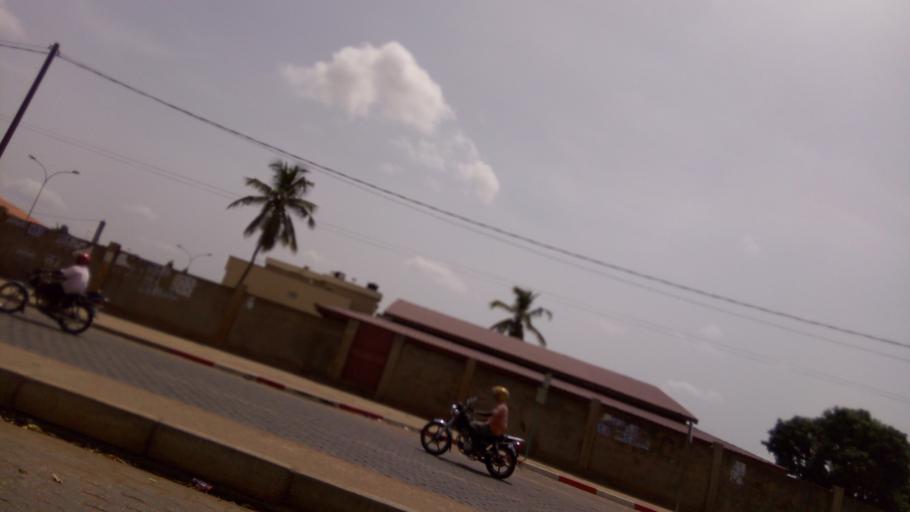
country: TG
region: Maritime
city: Lome
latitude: 6.1869
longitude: 1.1931
